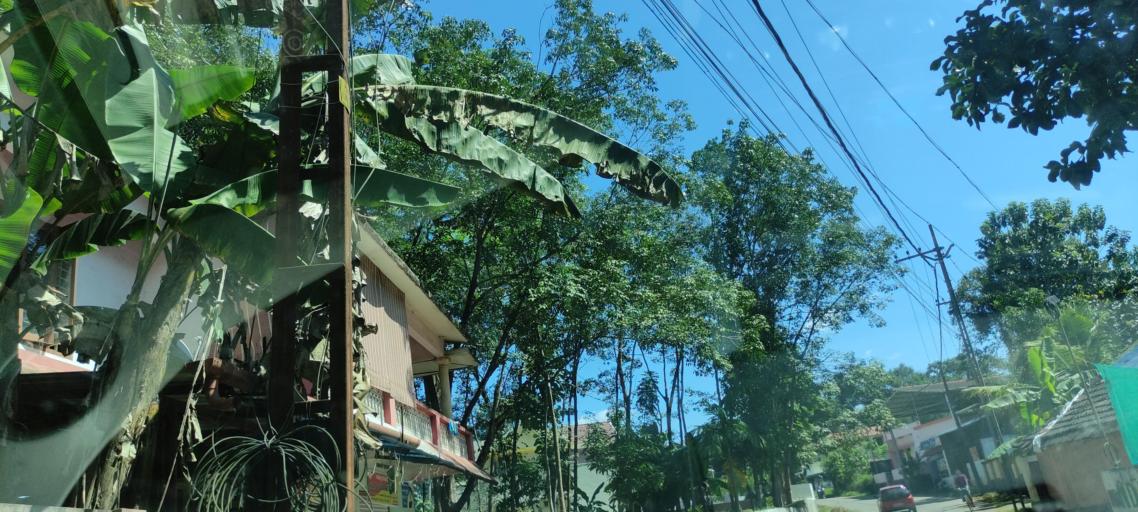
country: IN
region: Kerala
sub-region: Pattanamtitta
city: Adur
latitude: 9.0904
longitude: 76.6935
